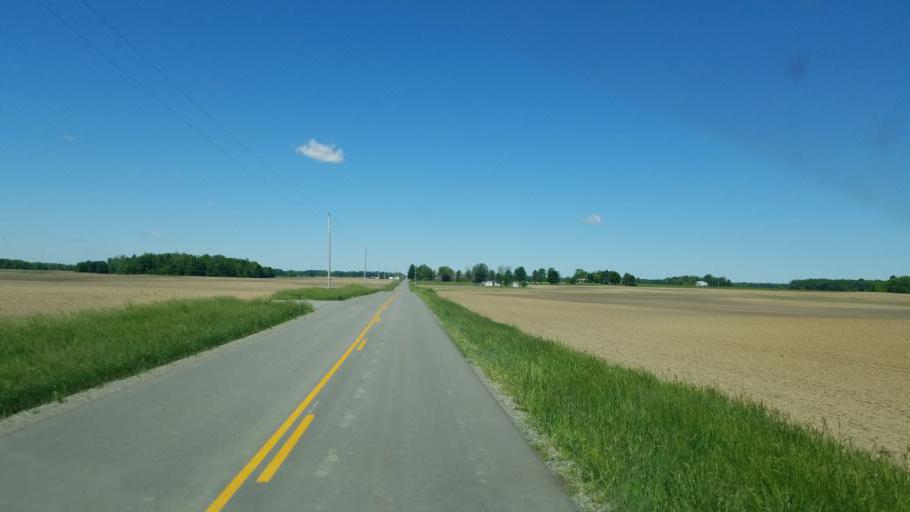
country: US
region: Ohio
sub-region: Logan County
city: Lakeview
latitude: 40.4174
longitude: -83.9613
